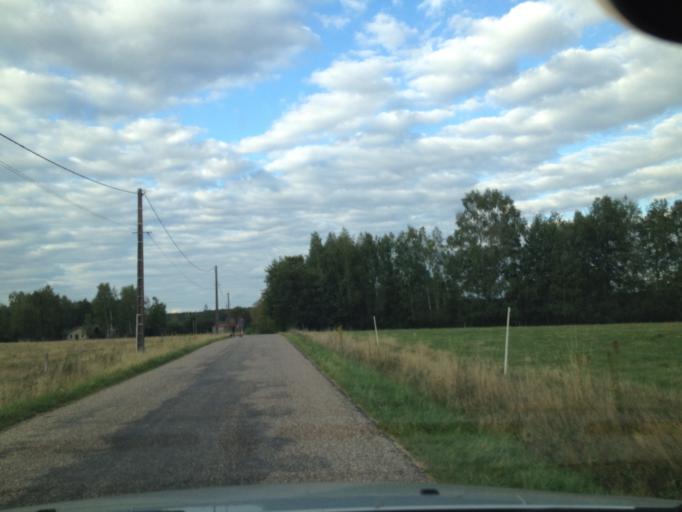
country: FR
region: Lorraine
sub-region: Departement des Vosges
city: Bains-les-Bains
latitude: 47.9930
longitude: 6.2092
